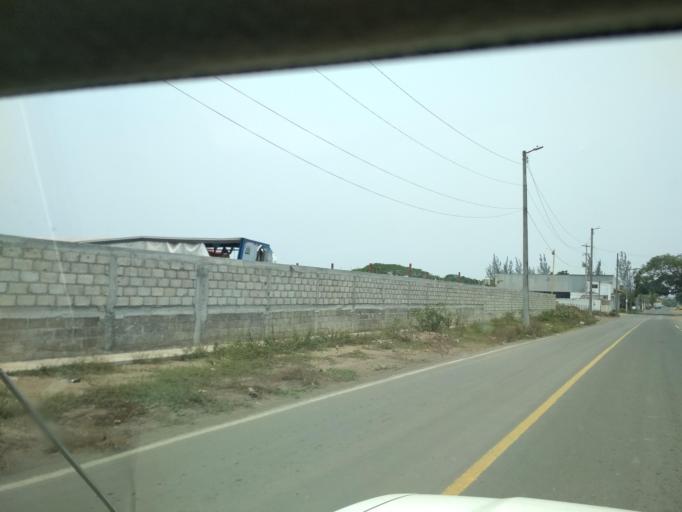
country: MX
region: Veracruz
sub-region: Veracruz
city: Delfino Victoria (Santa Fe)
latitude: 19.2091
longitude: -96.2661
